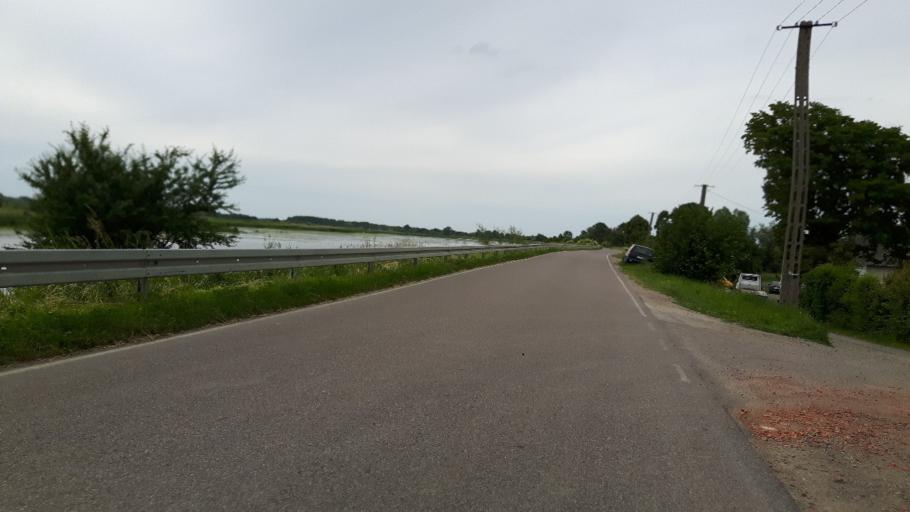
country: PL
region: Warmian-Masurian Voivodeship
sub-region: Powiat elblaski
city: Elblag
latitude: 54.1964
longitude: 19.3261
